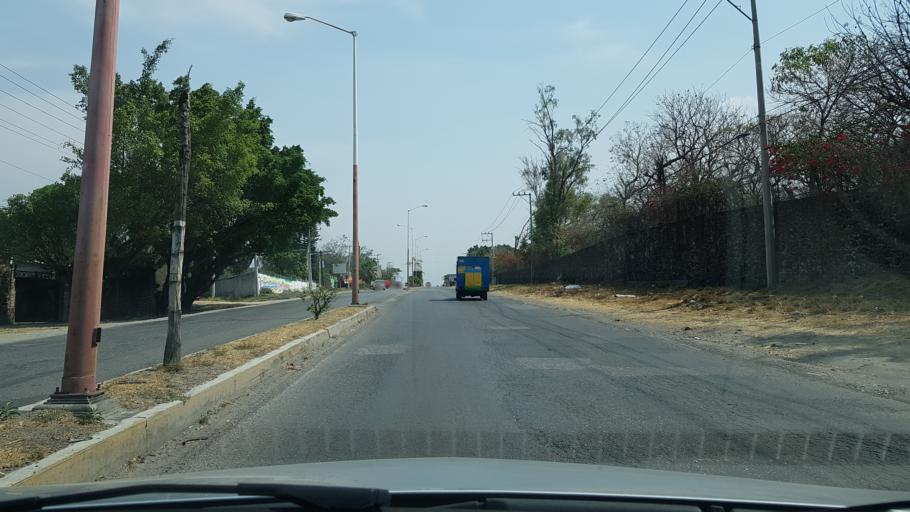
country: MX
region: Morelos
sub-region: Xochitepec
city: Chiconcuac
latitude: 18.7919
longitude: -99.2024
